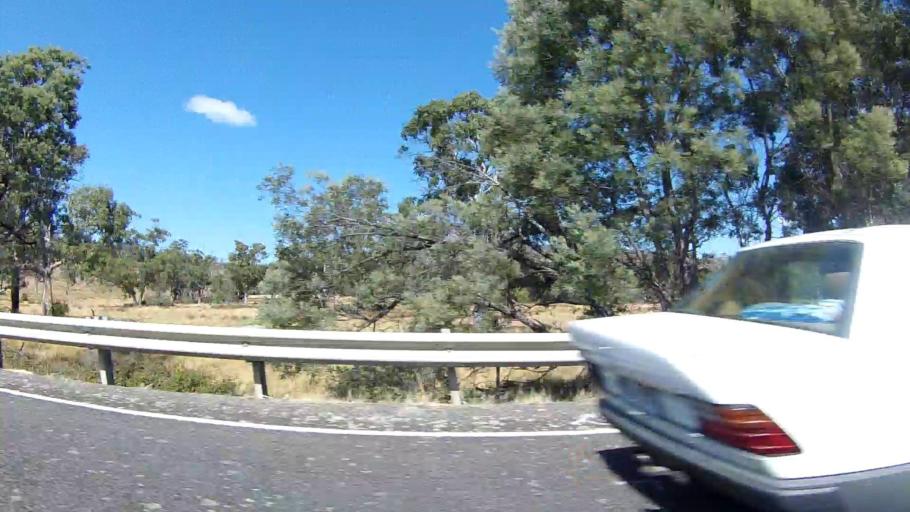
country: AU
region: Tasmania
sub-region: Sorell
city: Sorell
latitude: -42.5931
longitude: 147.7932
